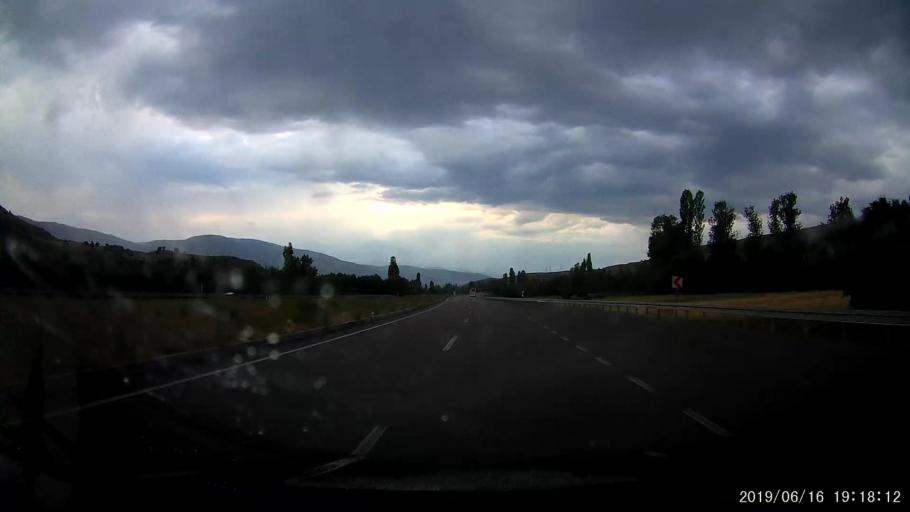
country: TR
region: Sivas
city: Akincilar
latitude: 40.0949
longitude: 38.4648
